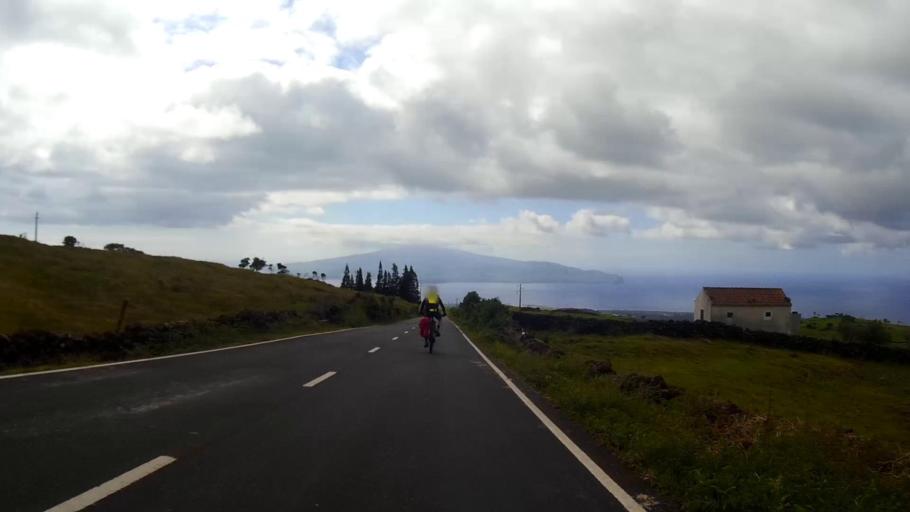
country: PT
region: Azores
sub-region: Madalena
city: Madalena
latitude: 38.4963
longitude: -28.4477
